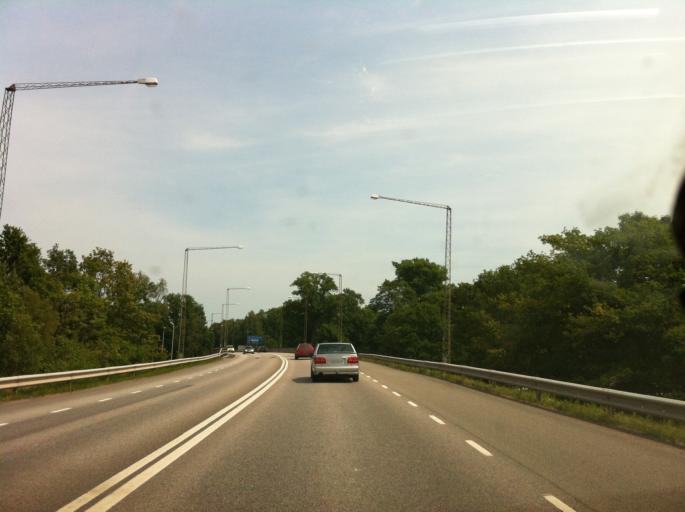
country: SE
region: Kalmar
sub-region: Kalmar Kommun
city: Kalmar
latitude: 56.6823
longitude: 16.3417
